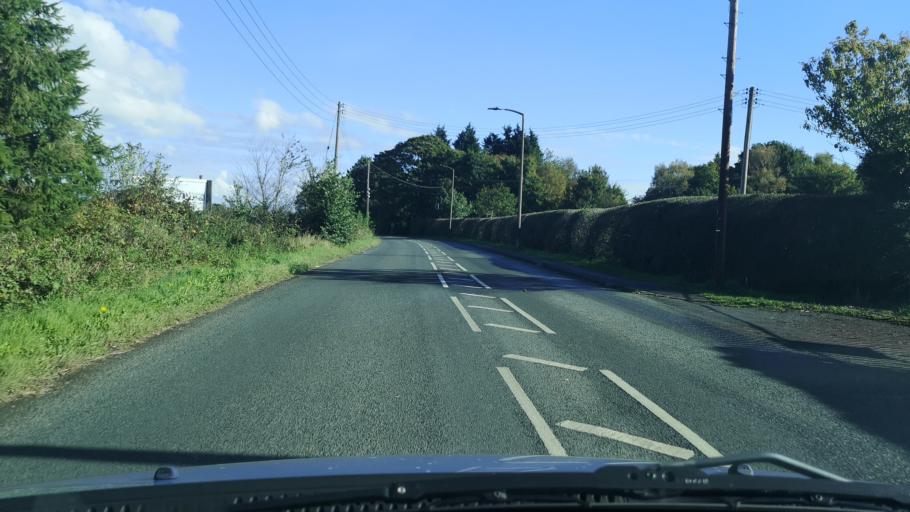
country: GB
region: England
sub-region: Doncaster
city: Askern
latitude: 53.6174
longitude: -1.1386
